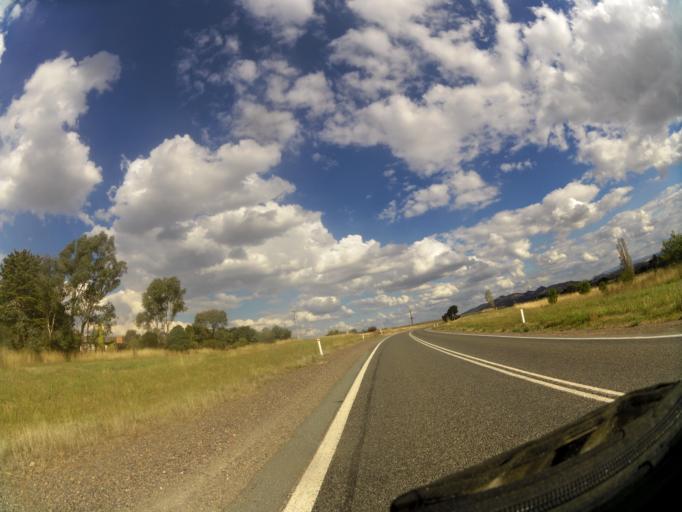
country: AU
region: Victoria
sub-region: Mansfield
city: Mansfield
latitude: -37.0213
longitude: 146.0936
